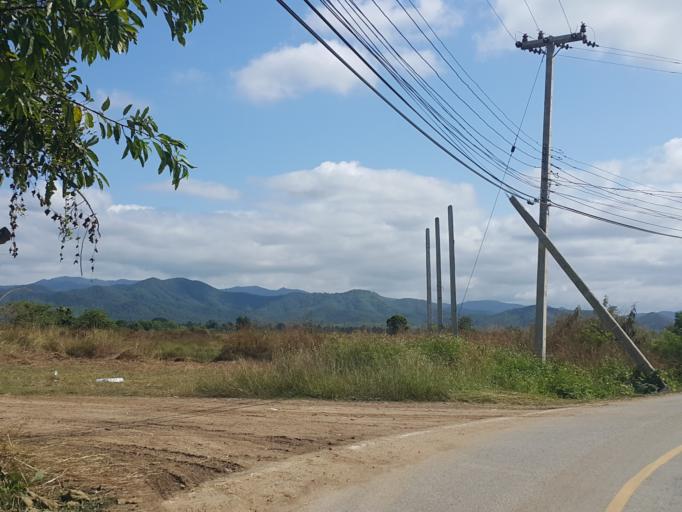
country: TH
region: Lamphun
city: Ban Thi
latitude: 18.5699
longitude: 99.0869
